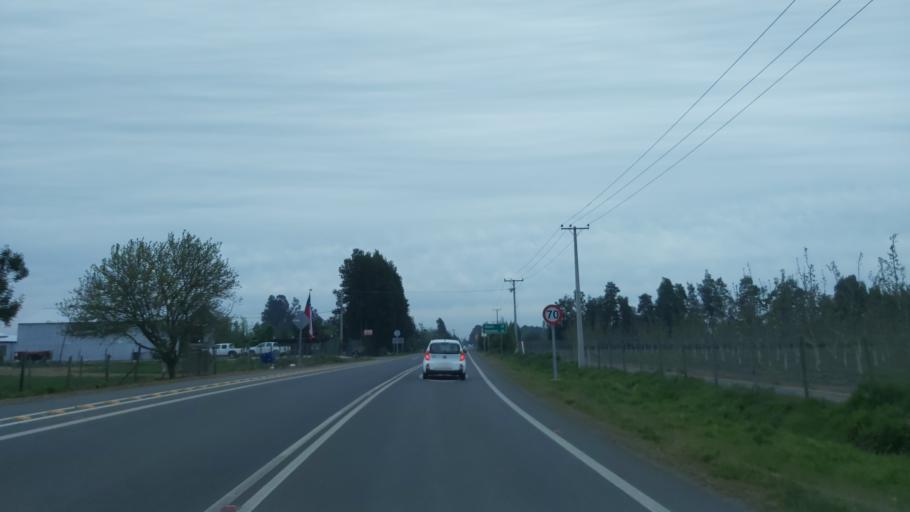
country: CL
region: Maule
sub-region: Provincia de Linares
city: Colbun
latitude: -35.7141
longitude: -71.4819
